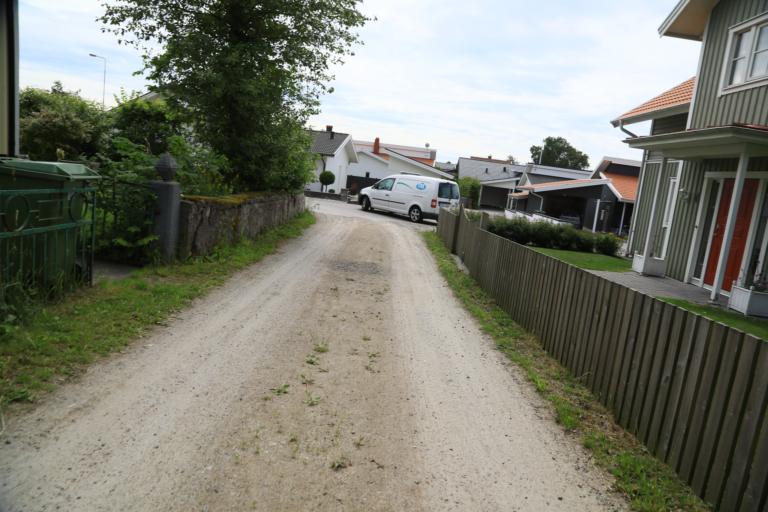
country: SE
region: Halland
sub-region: Varbergs Kommun
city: Varberg
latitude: 57.1280
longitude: 12.2685
